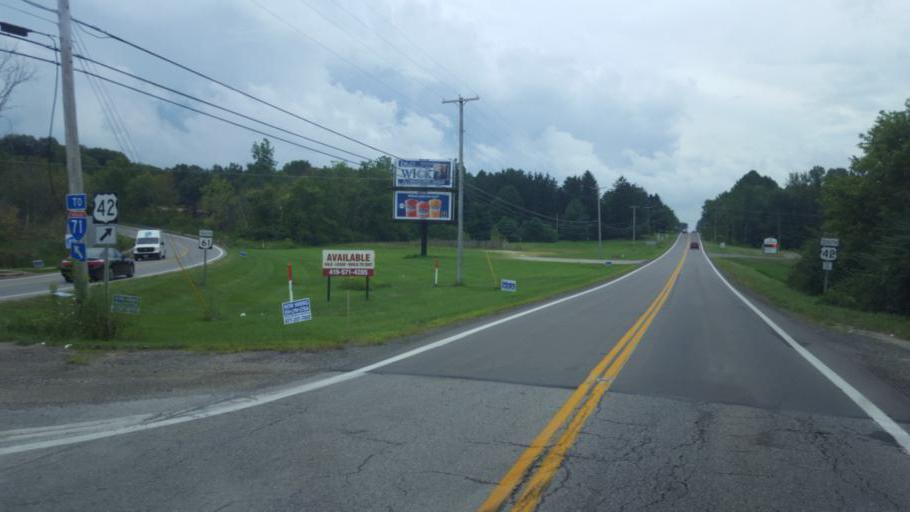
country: US
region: Ohio
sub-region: Morrow County
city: Mount Gilead
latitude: 40.5387
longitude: -82.8310
